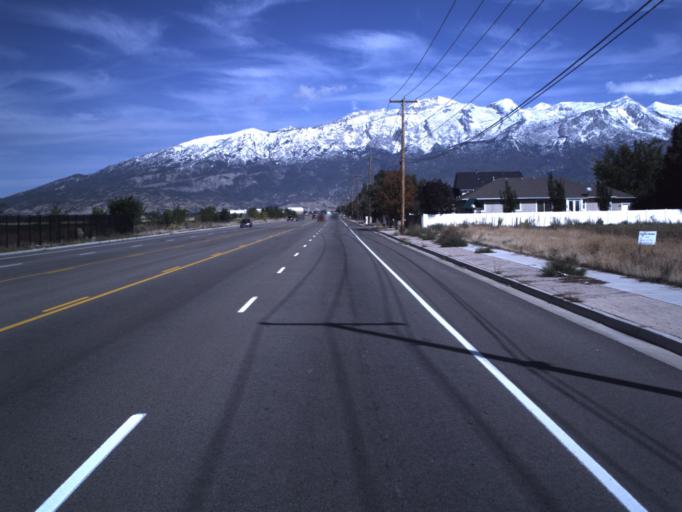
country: US
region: Utah
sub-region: Utah County
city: Cedar Hills
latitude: 40.4018
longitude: -111.7733
